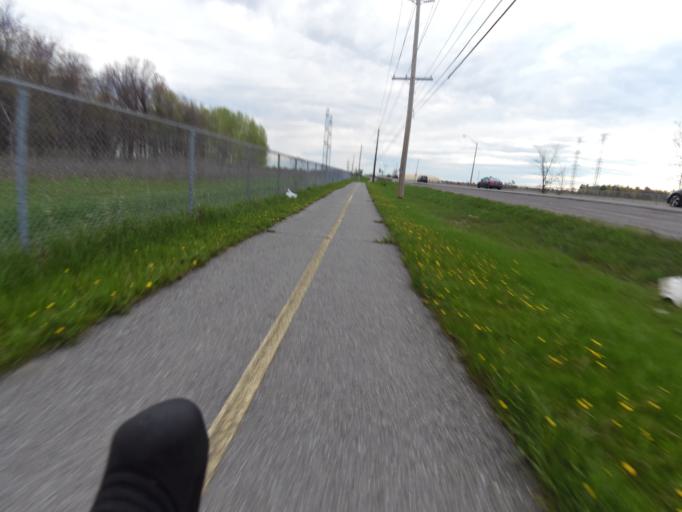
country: CA
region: Ontario
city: Bells Corners
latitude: 45.3160
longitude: -75.7734
